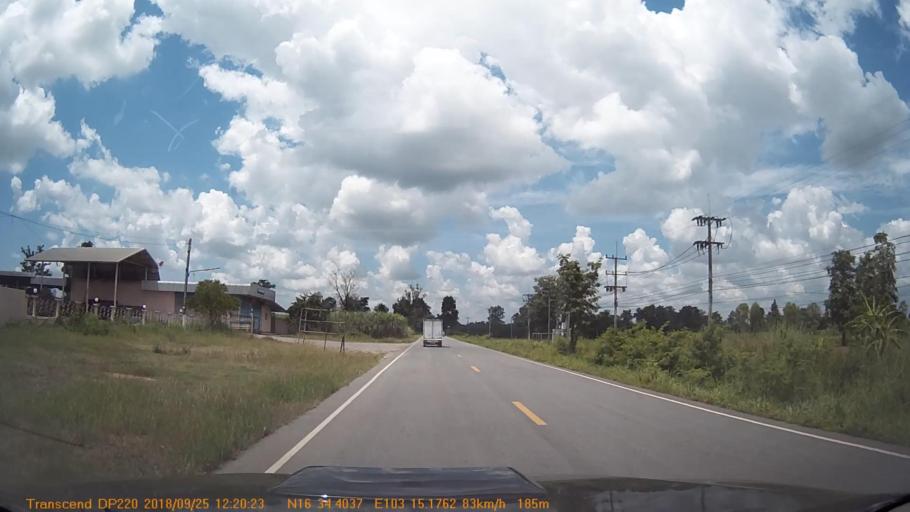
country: TH
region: Kalasin
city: Huai Mek
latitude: 16.5734
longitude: 103.2531
